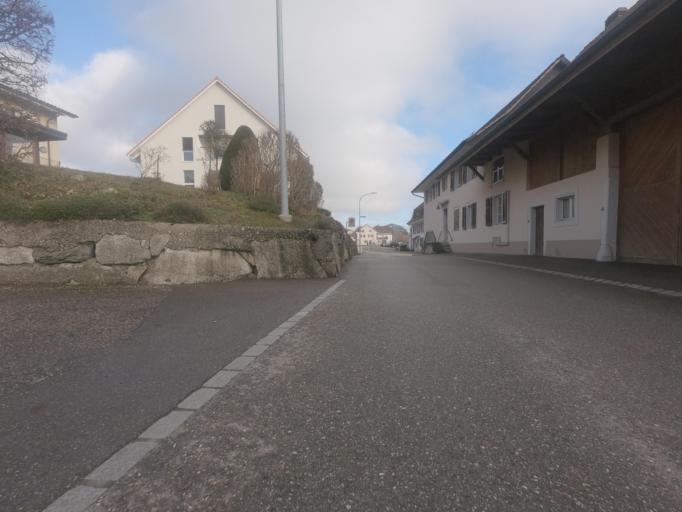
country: CH
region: Solothurn
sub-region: Bezirk Lebern
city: Langendorf
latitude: 47.2122
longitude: 7.4922
